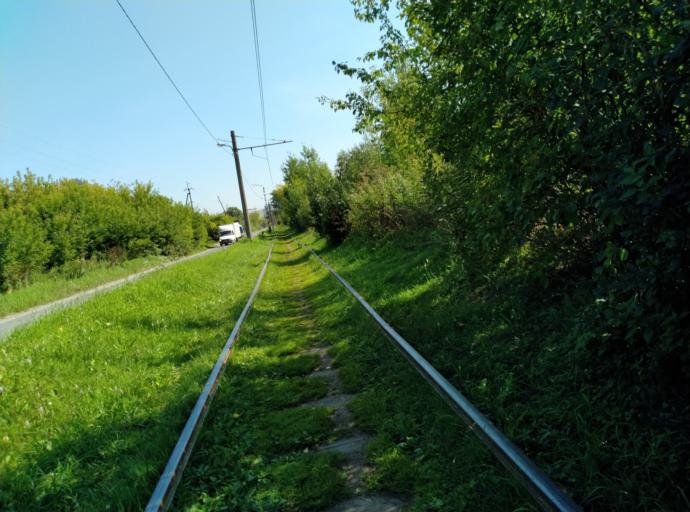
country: RU
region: Sverdlovsk
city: Shirokaya Rechka
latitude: 56.8386
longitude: 60.5221
